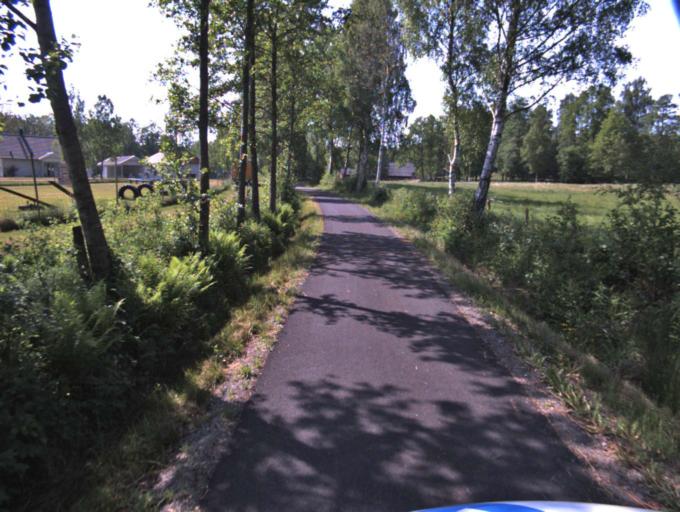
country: SE
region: Skane
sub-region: Kristianstads Kommun
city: Tollarp
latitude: 56.1991
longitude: 14.2861
